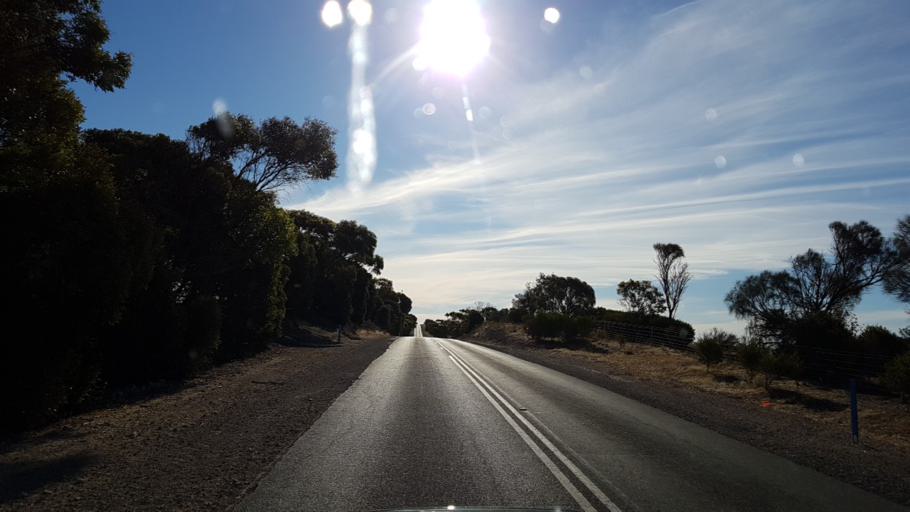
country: AU
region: South Australia
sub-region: Yorke Peninsula
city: Honiton
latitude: -34.9850
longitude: 137.2746
